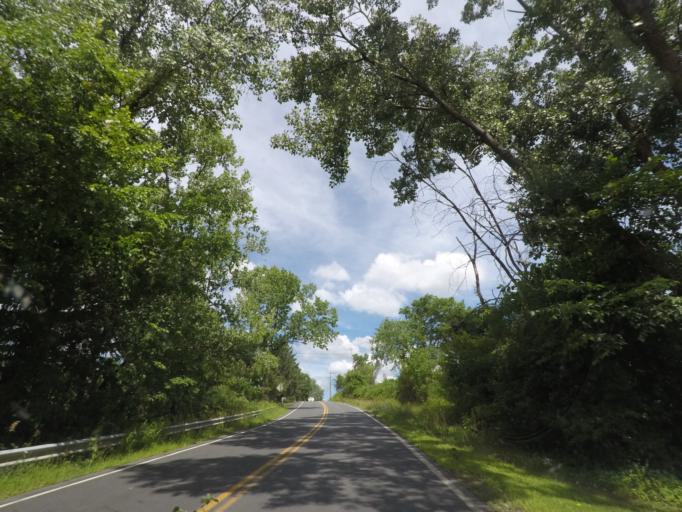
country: US
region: New York
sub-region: Rensselaer County
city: Wynantskill
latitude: 42.7159
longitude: -73.6469
